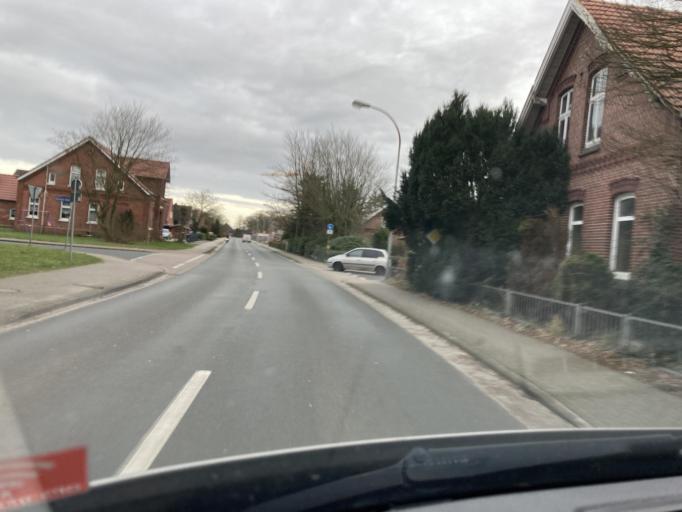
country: DE
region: Lower Saxony
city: Leer
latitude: 53.1645
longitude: 7.4554
